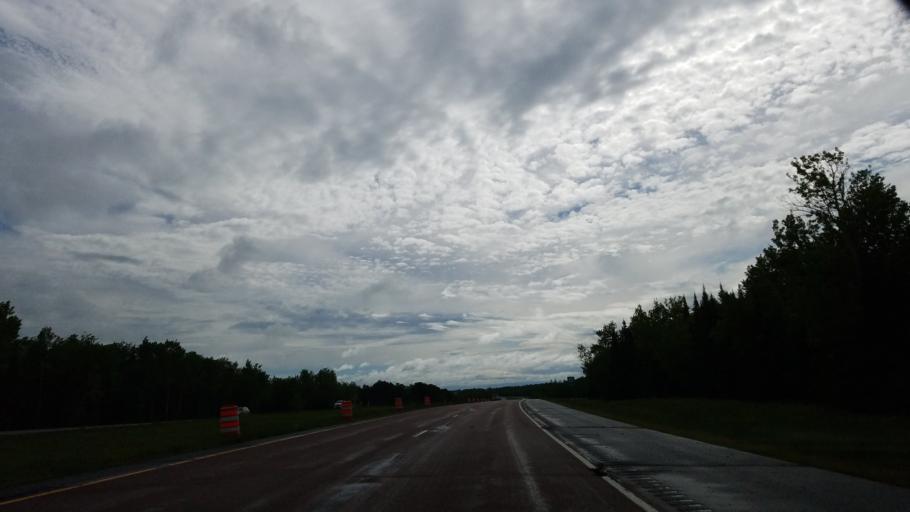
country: US
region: Minnesota
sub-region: Lake County
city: Two Harbors
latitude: 46.9276
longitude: -91.8506
